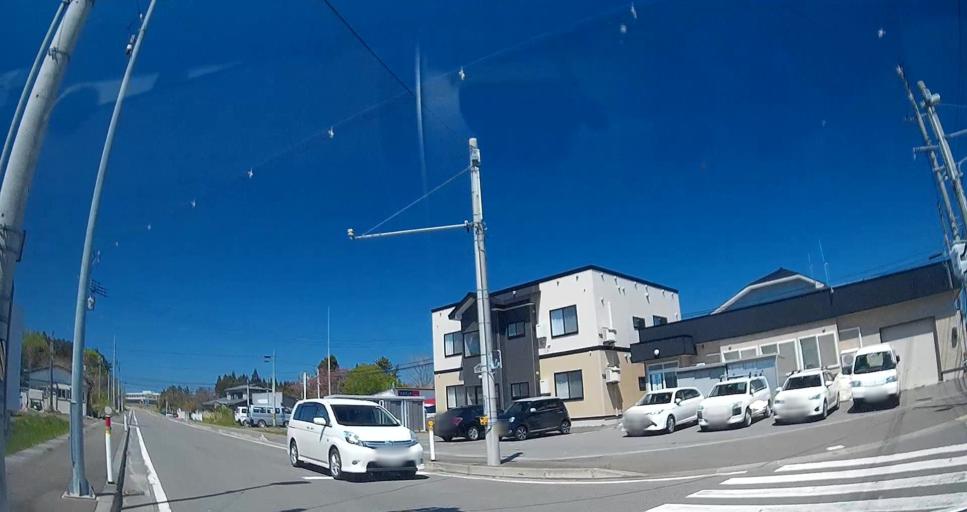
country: JP
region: Aomori
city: Misawa
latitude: 40.9686
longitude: 141.3748
